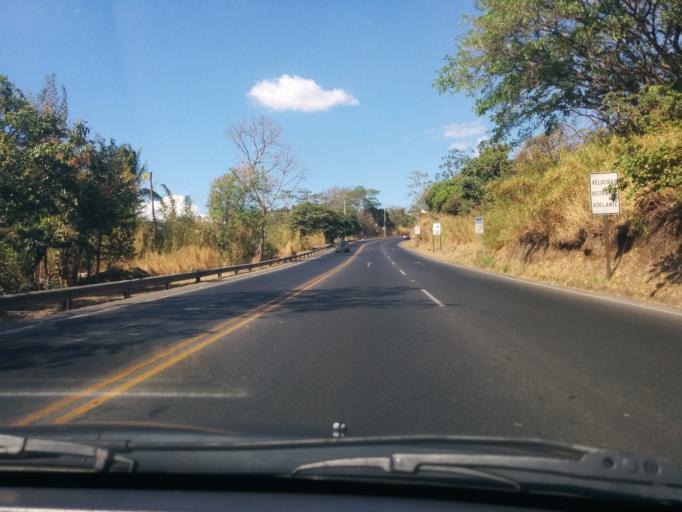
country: CR
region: Alajuela
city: Carrillos
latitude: 10.0034
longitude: -84.3003
